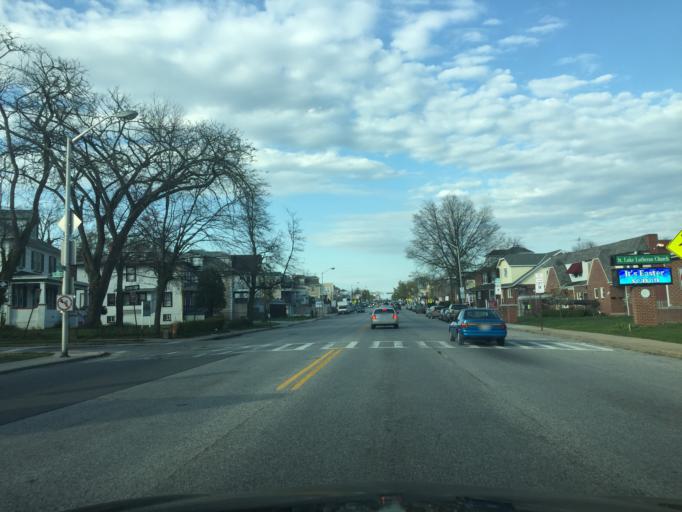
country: US
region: Maryland
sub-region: Baltimore County
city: Parkville
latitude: 39.3664
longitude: -76.5492
